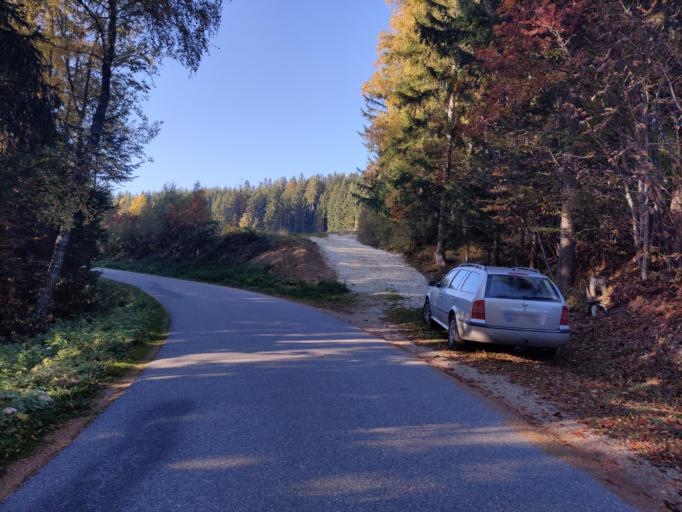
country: AT
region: Styria
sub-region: Politischer Bezirk Hartberg-Fuerstenfeld
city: Sankt Jakob im Walde
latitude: 47.4673
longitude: 15.8058
